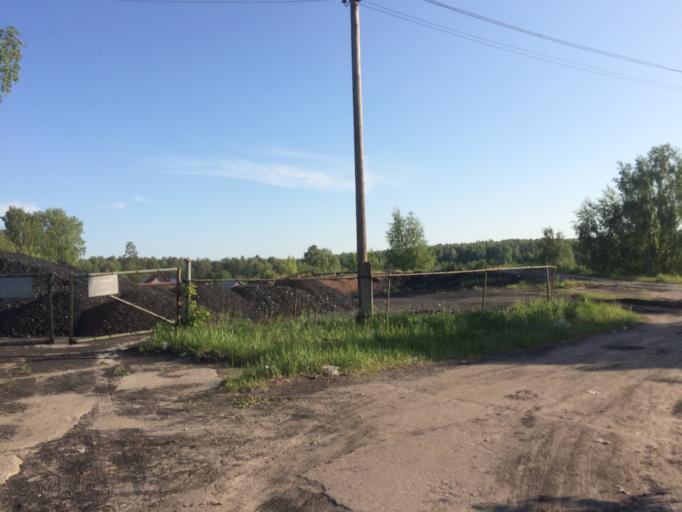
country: RU
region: Mariy-El
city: Mochalishche
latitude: 56.5425
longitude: 48.4025
